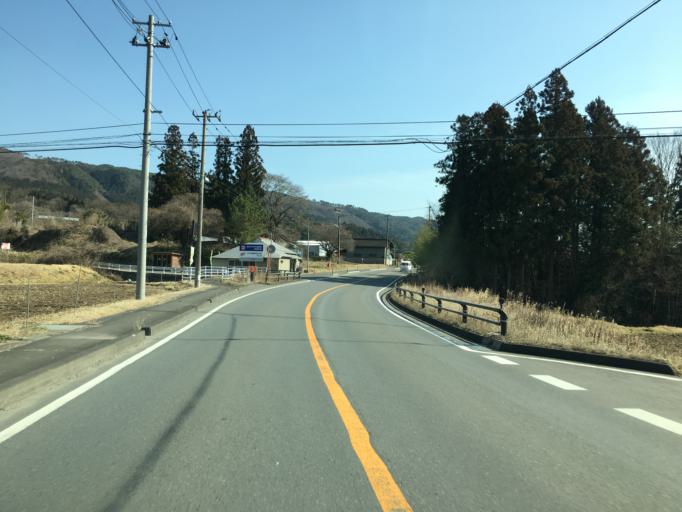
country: JP
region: Ibaraki
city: Daigo
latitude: 36.8377
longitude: 140.4480
